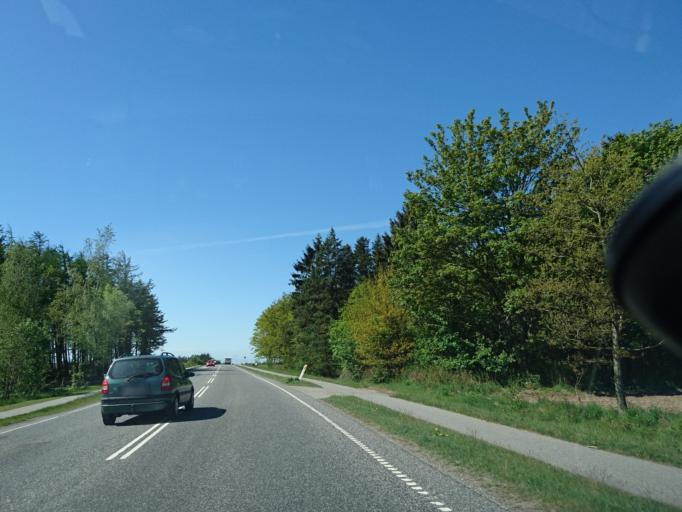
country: DK
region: North Denmark
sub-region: Hjorring Kommune
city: Sindal
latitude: 57.4615
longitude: 10.1499
